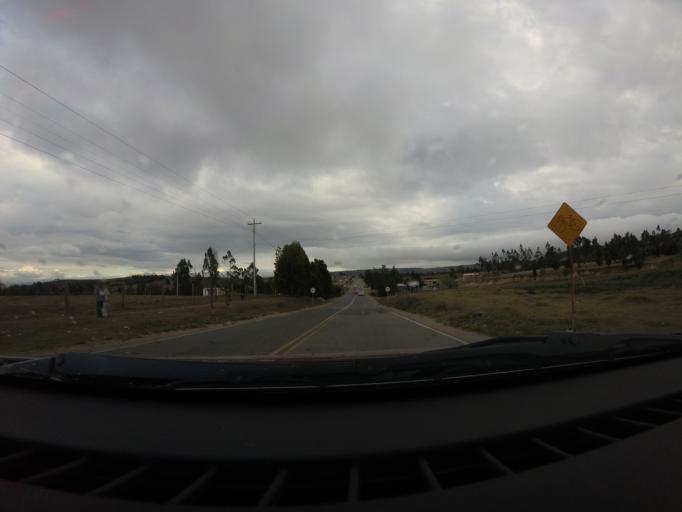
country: CO
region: Boyaca
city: Tunja
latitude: 5.5489
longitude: -73.4037
